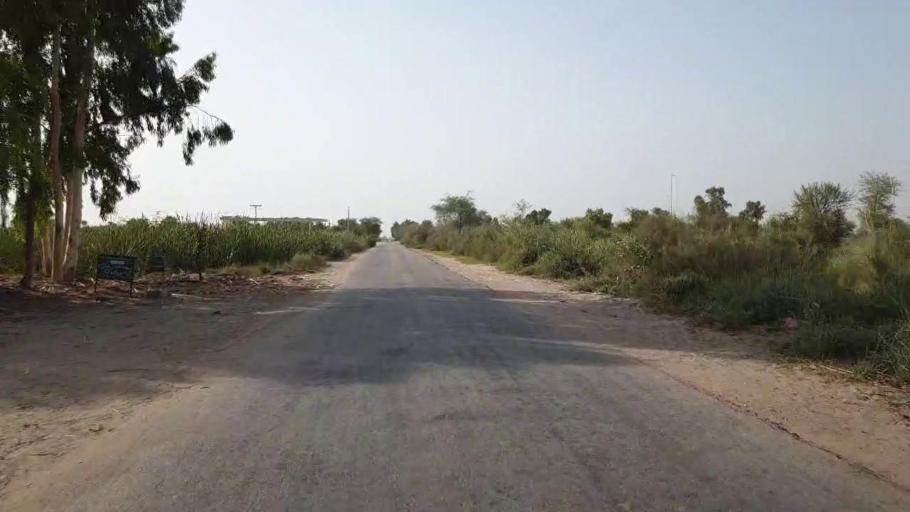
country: PK
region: Sindh
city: Khadro
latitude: 26.3344
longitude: 68.9285
